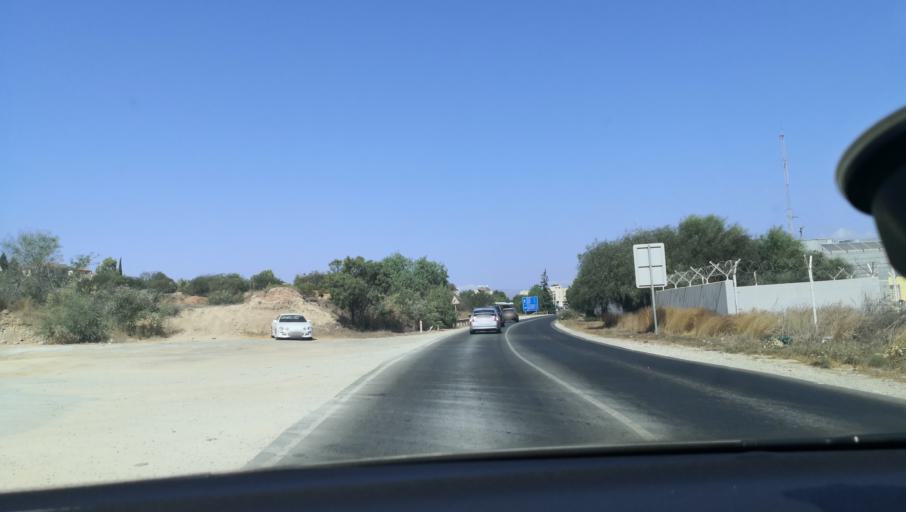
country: CY
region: Lefkosia
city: Kato Deftera
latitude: 35.1102
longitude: 33.2845
